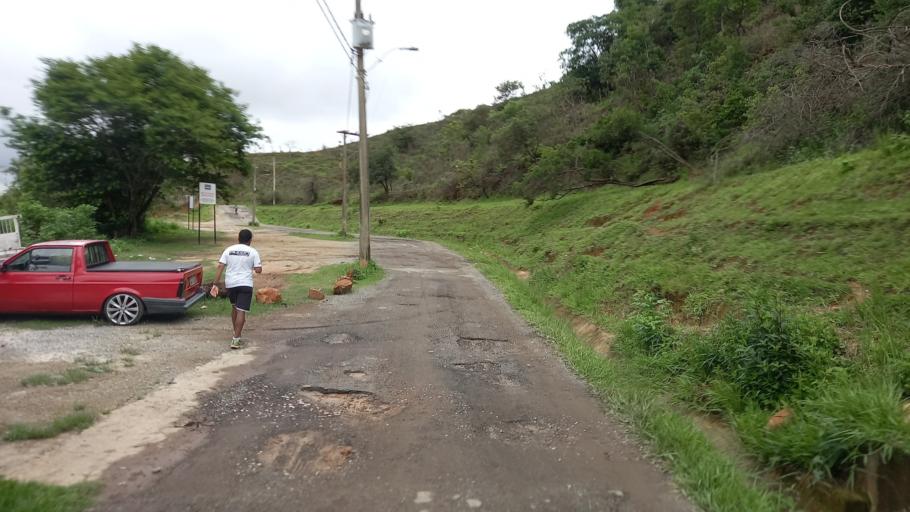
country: BR
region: Minas Gerais
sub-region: Belo Horizonte
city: Belo Horizonte
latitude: -19.9210
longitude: -43.8861
